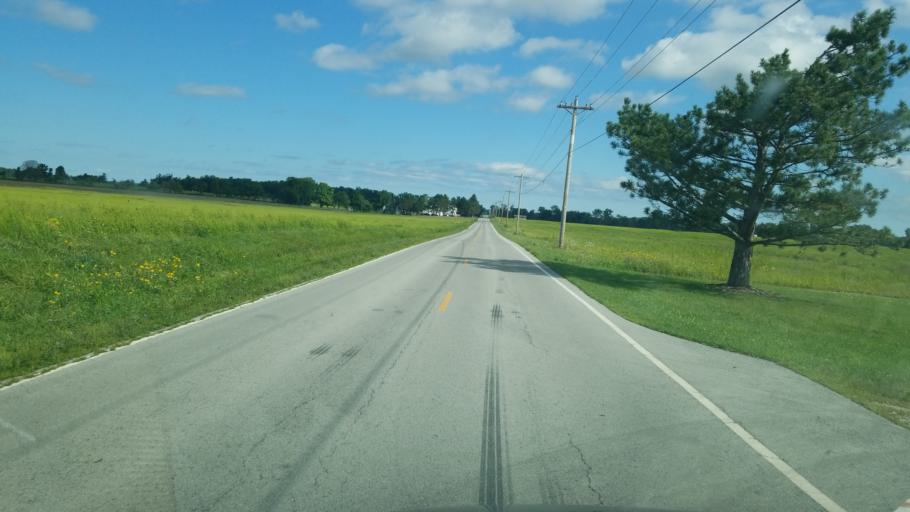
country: US
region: Ohio
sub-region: Seneca County
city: Fostoria
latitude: 41.0966
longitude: -83.4403
